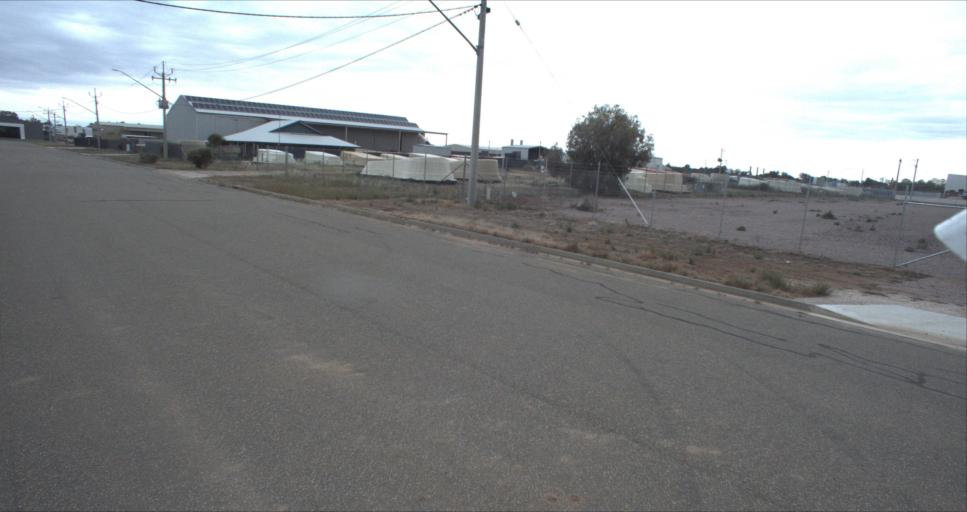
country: AU
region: New South Wales
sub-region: Leeton
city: Leeton
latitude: -34.5439
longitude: 146.3899
